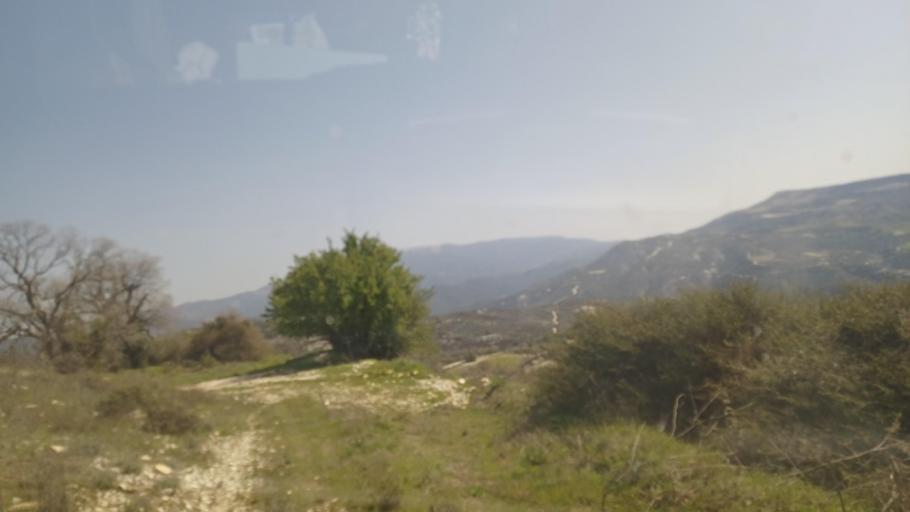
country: CY
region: Limassol
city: Pachna
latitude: 34.8691
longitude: 32.7083
